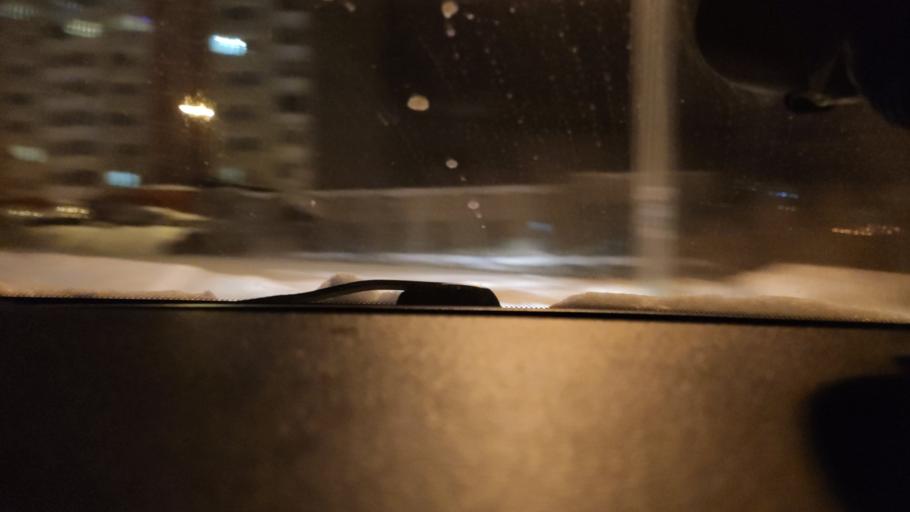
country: RU
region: Perm
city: Perm
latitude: 58.0577
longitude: 56.3465
